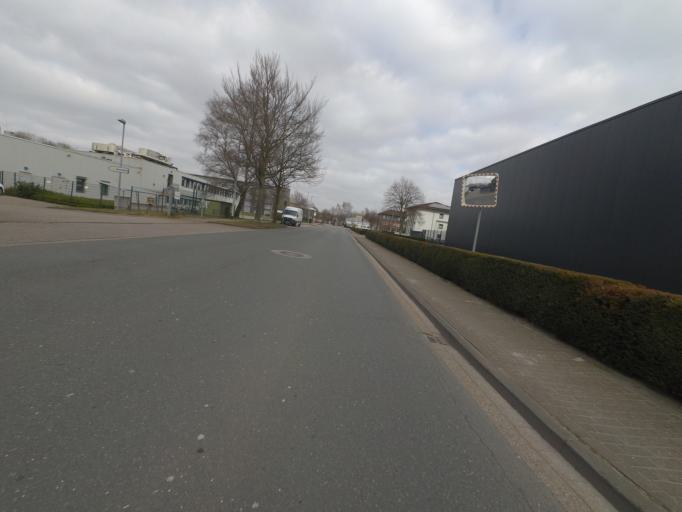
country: DE
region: Lower Saxony
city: Oldenburg
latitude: 53.1110
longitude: 8.2565
